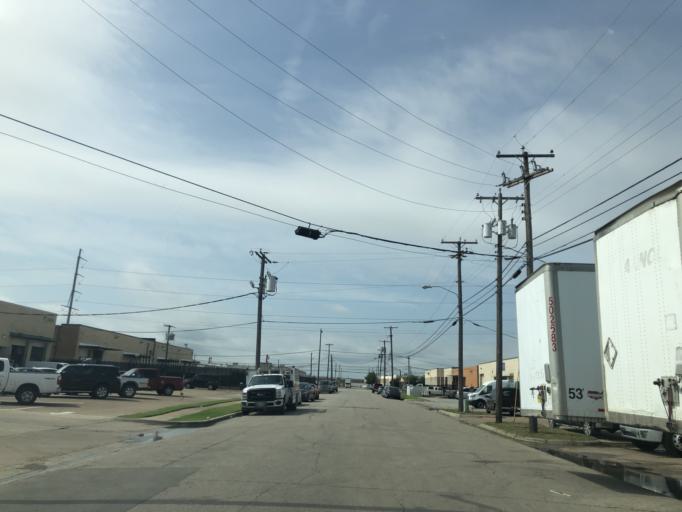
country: US
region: Texas
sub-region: Dallas County
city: Dallas
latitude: 32.8099
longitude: -96.8716
